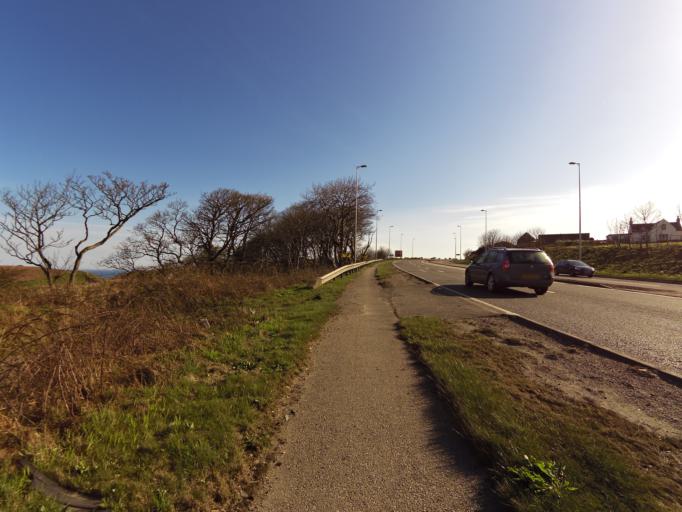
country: GB
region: Scotland
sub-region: Aberdeenshire
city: Newtonhill
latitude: 57.0069
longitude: -2.1737
